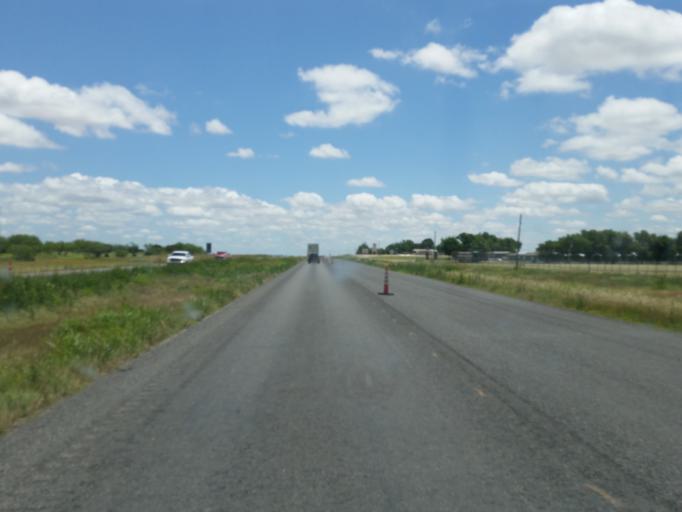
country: US
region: Texas
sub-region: Scurry County
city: Snyder
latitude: 32.7261
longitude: -100.8929
